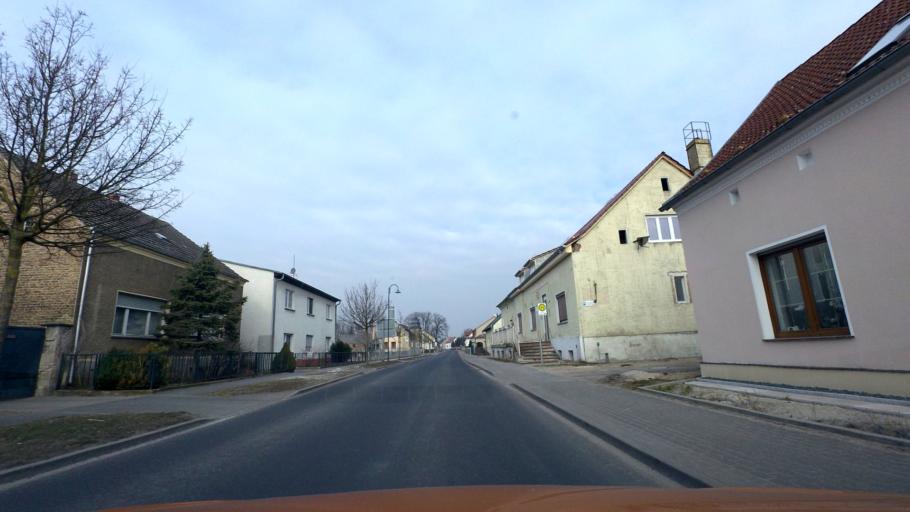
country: DE
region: Brandenburg
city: Trebbin
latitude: 52.2181
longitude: 13.2018
